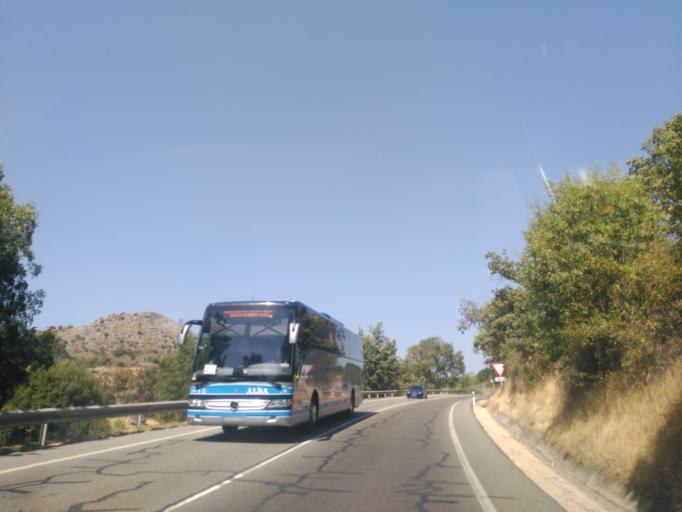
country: ES
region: Castille and Leon
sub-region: Provincia de Salamanca
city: Vallejera de Riofrio
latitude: 40.3947
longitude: -5.7396
